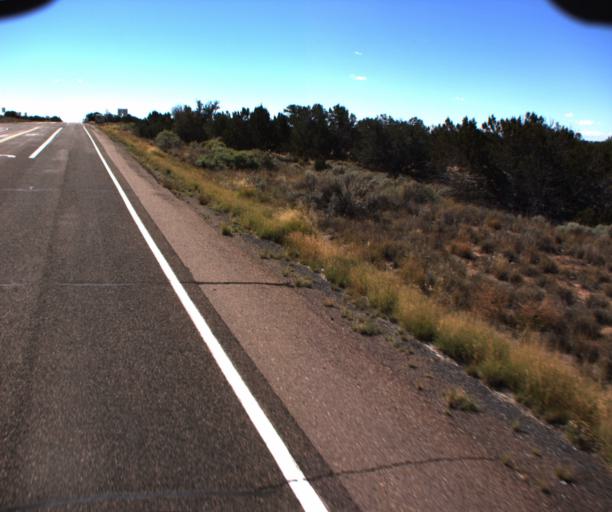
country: US
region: Arizona
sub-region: Apache County
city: Houck
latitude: 34.9035
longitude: -109.2381
